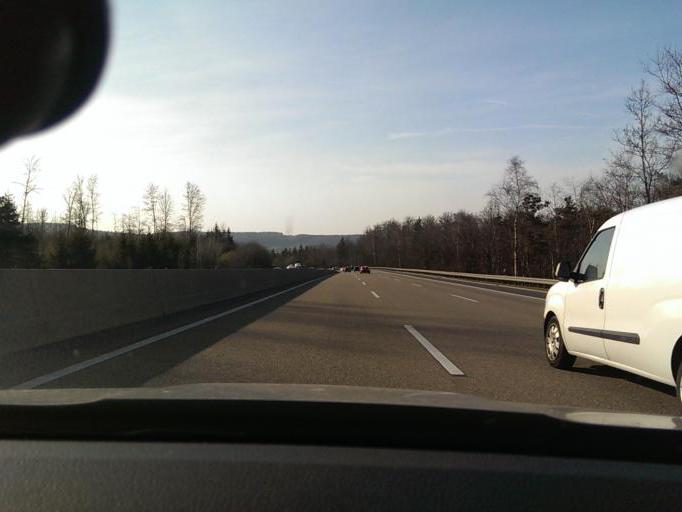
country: DE
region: Hesse
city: Schwarzenborn
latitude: 50.9554
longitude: 9.5029
